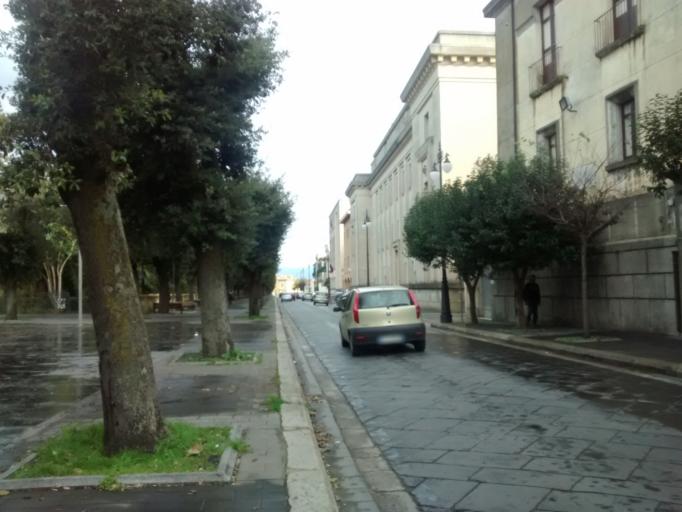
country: IT
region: Calabria
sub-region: Provincia di Vibo-Valentia
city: Vibo Valentia
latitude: 38.6744
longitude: 16.1057
